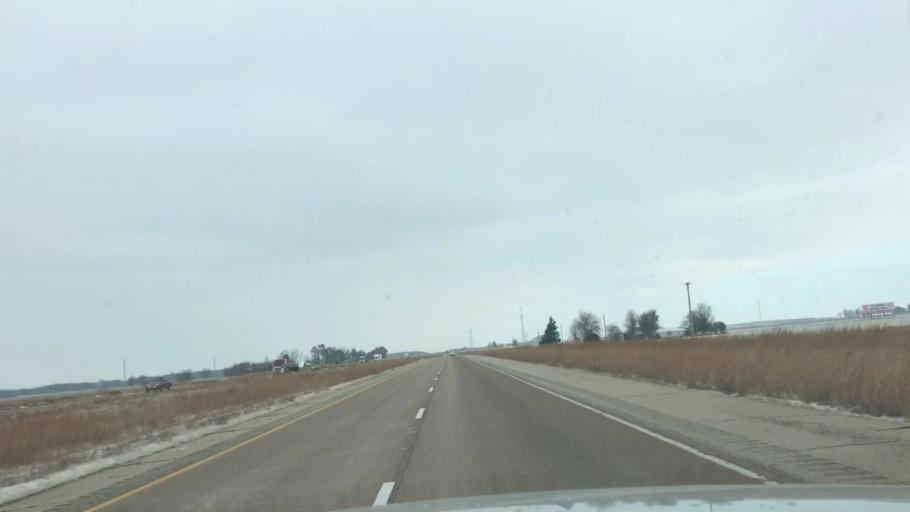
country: US
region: Illinois
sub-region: Montgomery County
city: Raymond
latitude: 39.4059
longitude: -89.6431
